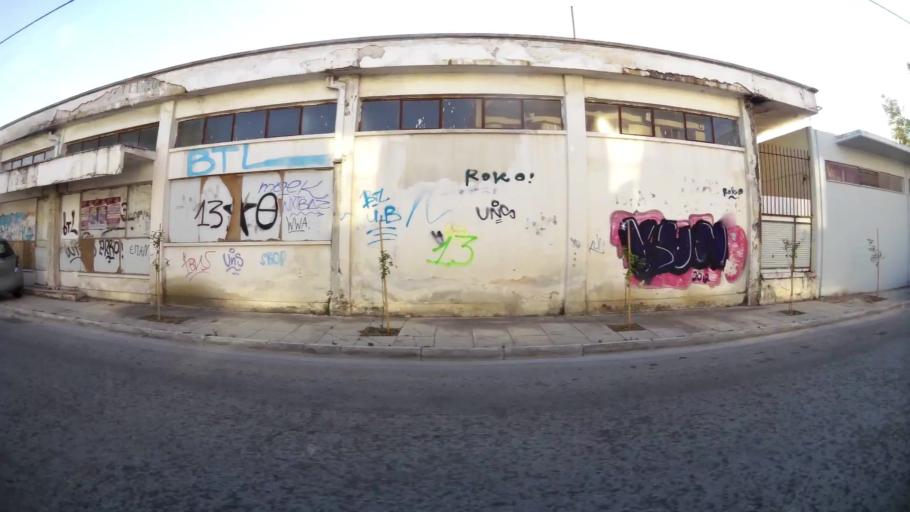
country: GR
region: Attica
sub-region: Nomarchia Anatolikis Attikis
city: Koropi
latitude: 37.9099
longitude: 23.8736
